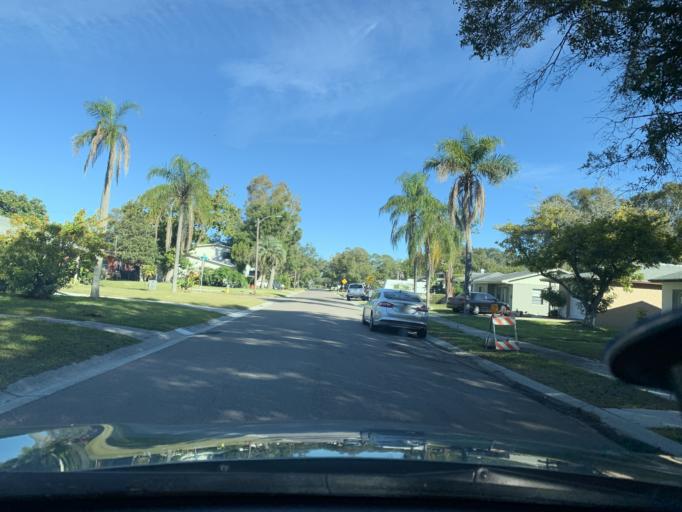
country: US
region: Florida
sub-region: Pinellas County
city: Gulfport
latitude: 27.7489
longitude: -82.6940
